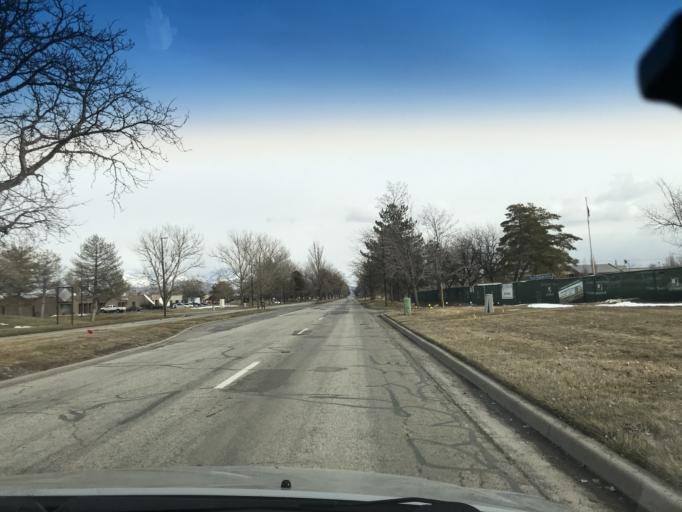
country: US
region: Utah
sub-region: Salt Lake County
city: West Valley City
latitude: 40.7763
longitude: -112.0157
